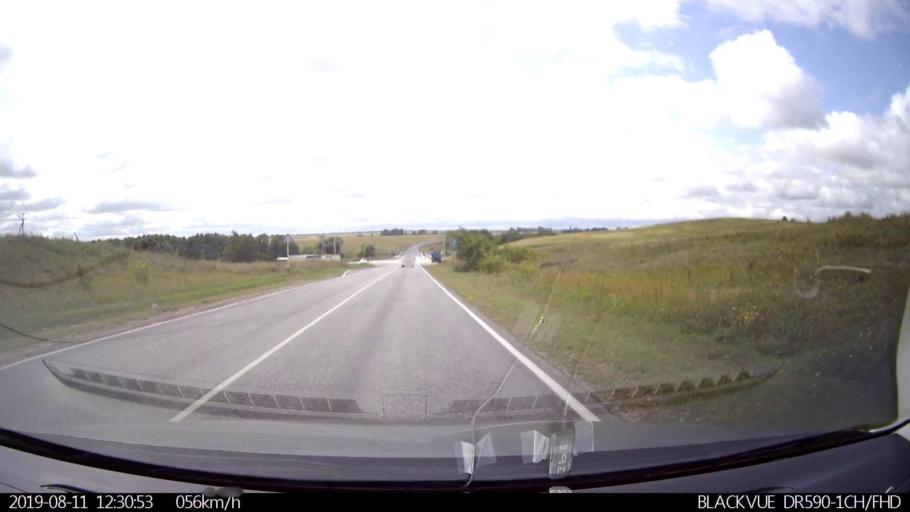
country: RU
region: Ulyanovsk
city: Ignatovka
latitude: 53.8227
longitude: 47.8904
